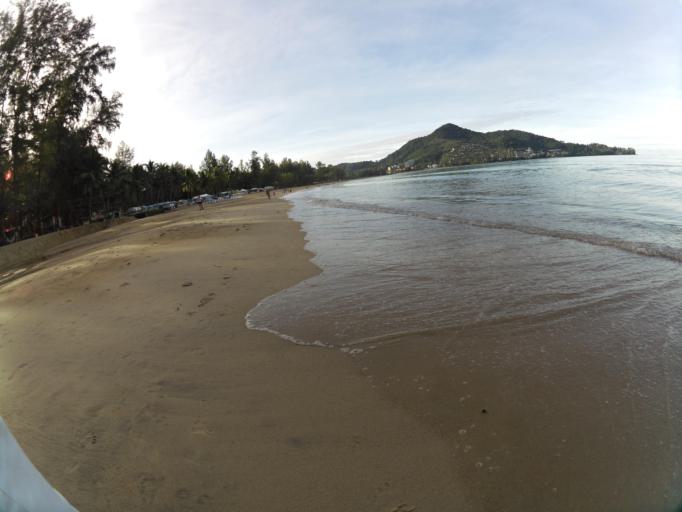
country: TH
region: Phuket
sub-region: Amphoe Kathu
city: Kathu
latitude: 7.9611
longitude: 98.2834
